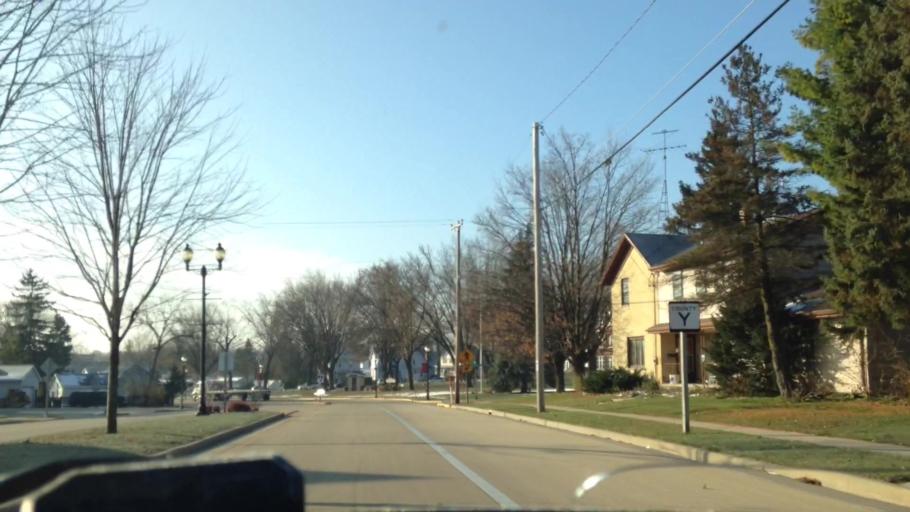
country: US
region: Wisconsin
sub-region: Dodge County
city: Mayville
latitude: 43.4995
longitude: -88.5449
